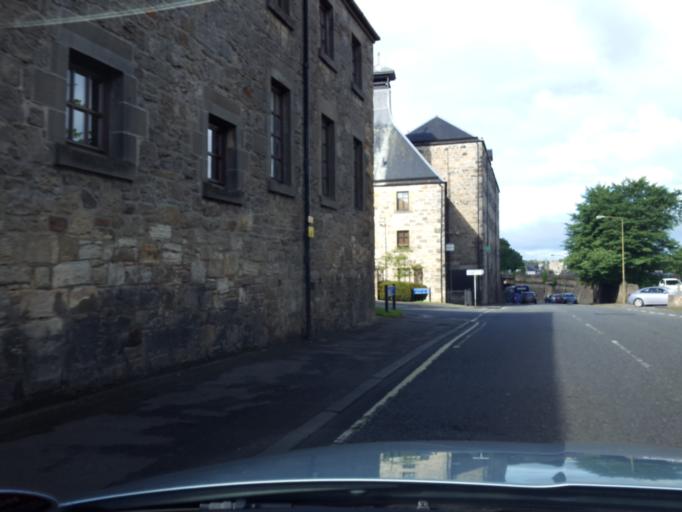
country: GB
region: Scotland
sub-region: West Lothian
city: Linlithgow
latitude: 55.9767
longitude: -3.5910
